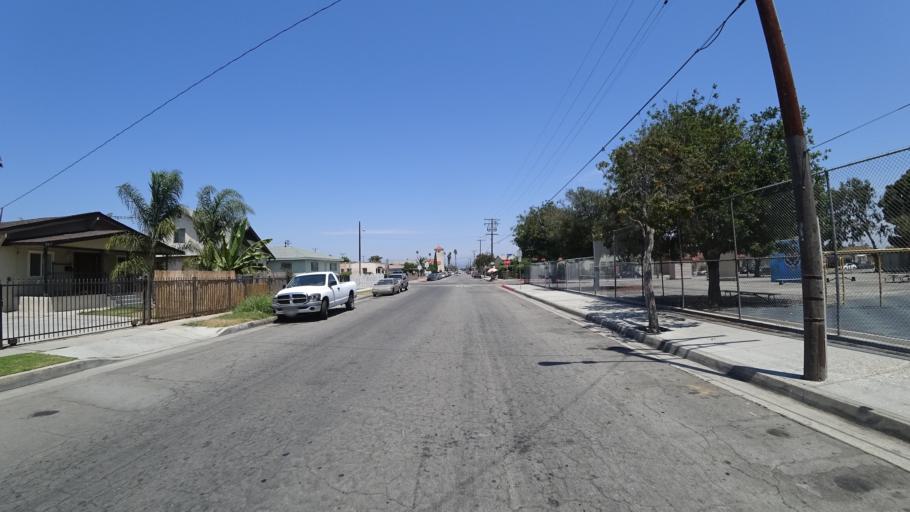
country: US
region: California
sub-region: Los Angeles County
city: Westmont
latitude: 33.9492
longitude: -118.2959
